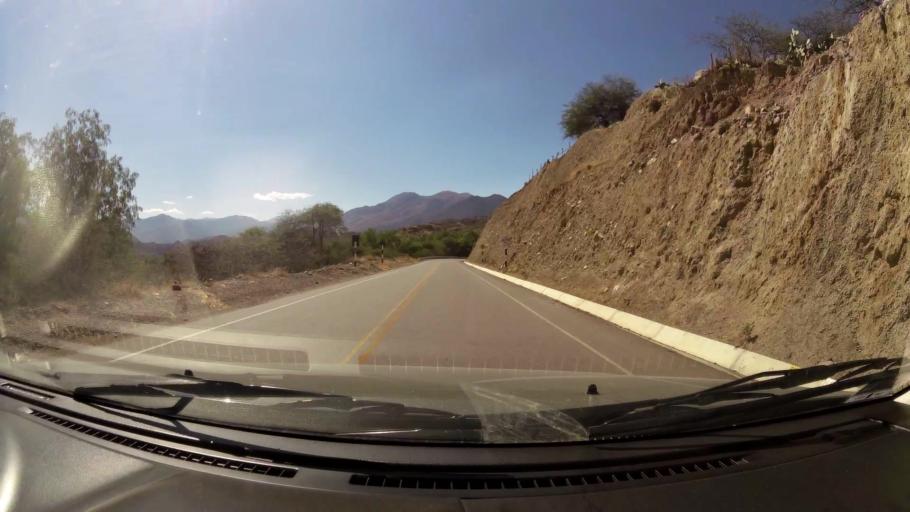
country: PE
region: Ayacucho
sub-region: Provincia de Huanta
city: Luricocha
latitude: -12.8877
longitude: -74.3164
